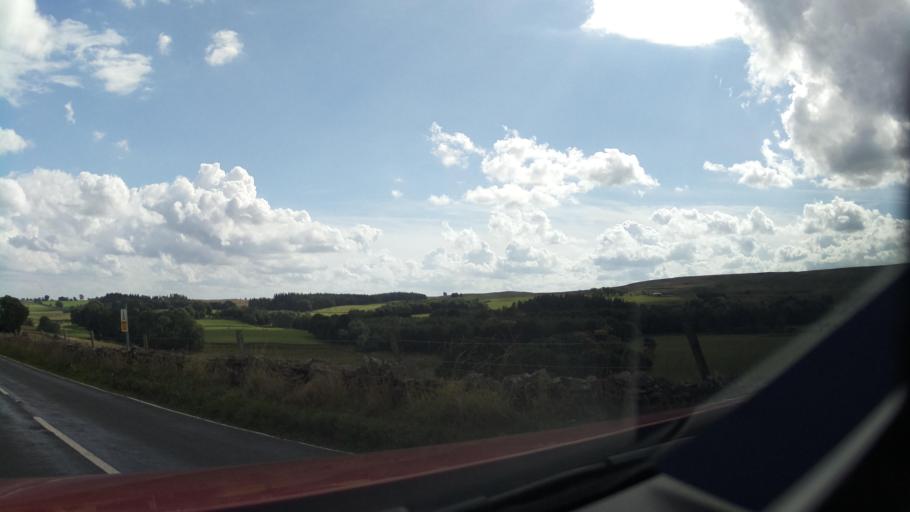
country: GB
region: England
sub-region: North Yorkshire
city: Leyburn
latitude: 54.3676
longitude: -1.8276
